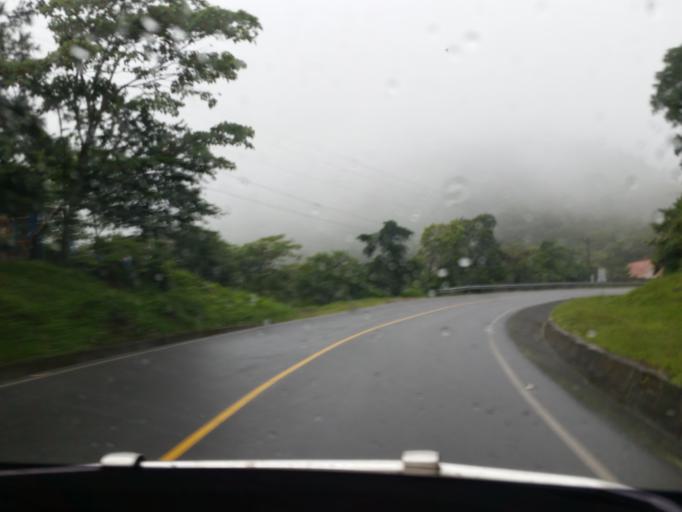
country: NI
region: Matagalpa
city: Matagalpa
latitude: 12.9754
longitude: -85.9209
